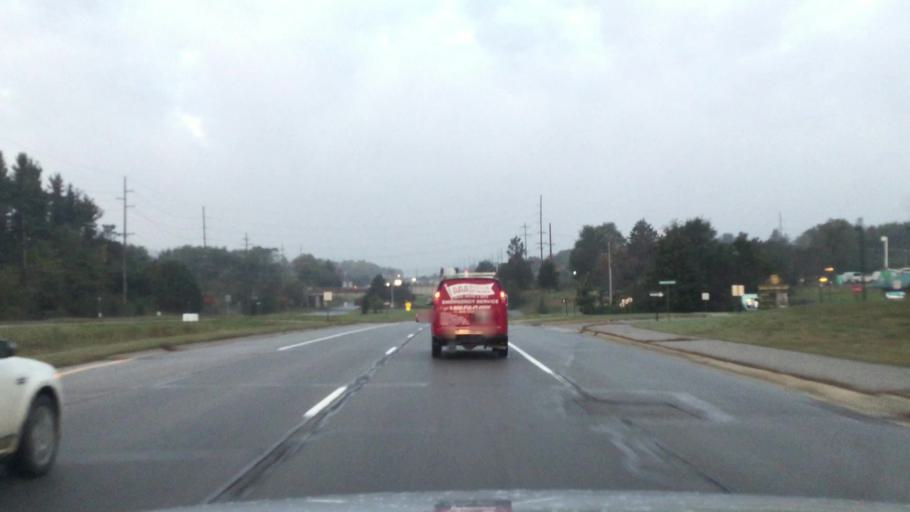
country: US
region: Michigan
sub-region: Oakland County
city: Milford
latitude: 42.6421
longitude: -83.6122
